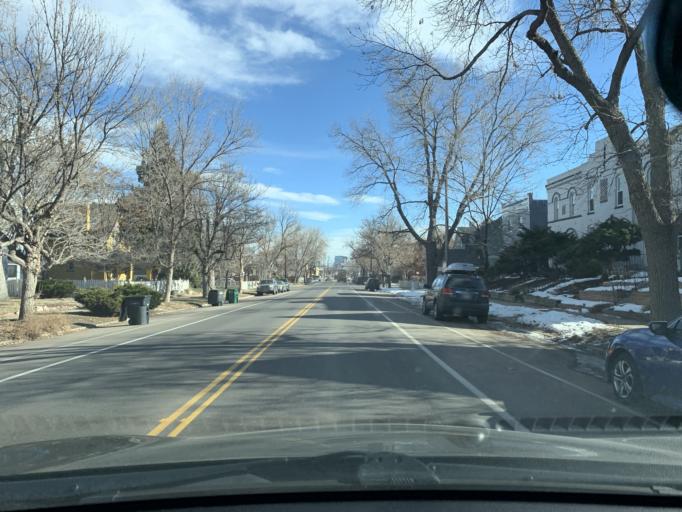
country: US
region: Colorado
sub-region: Jefferson County
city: Edgewater
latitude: 39.7512
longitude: -105.0280
